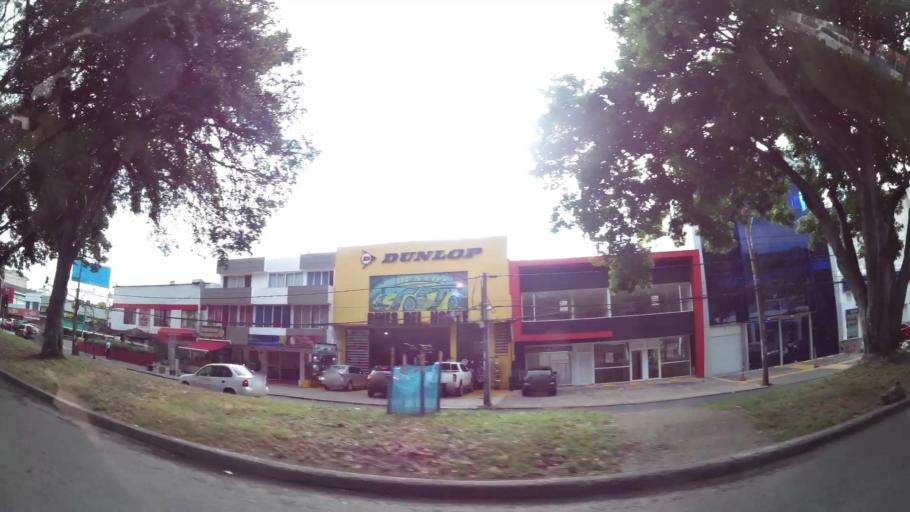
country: CO
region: Valle del Cauca
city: Cali
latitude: 3.4799
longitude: -76.5252
